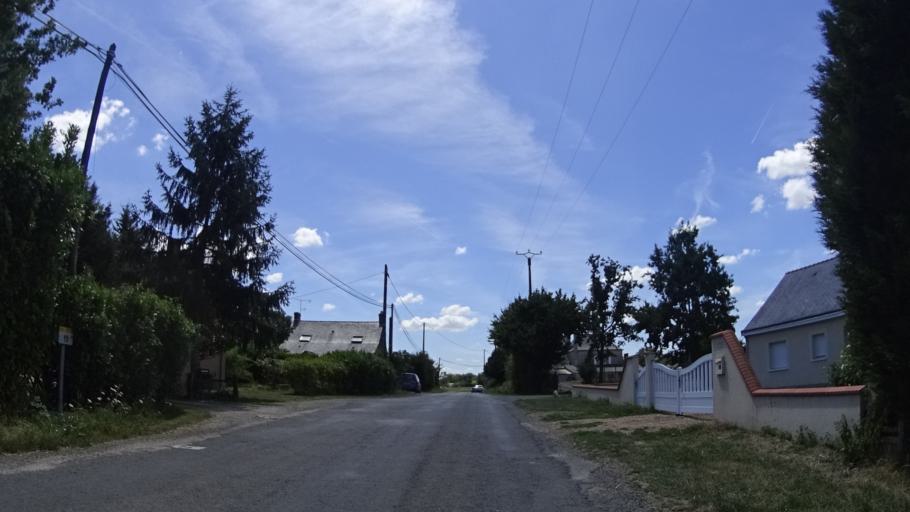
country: FR
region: Pays de la Loire
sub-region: Departement de Maine-et-Loire
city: Segre
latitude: 47.6142
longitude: -0.8952
